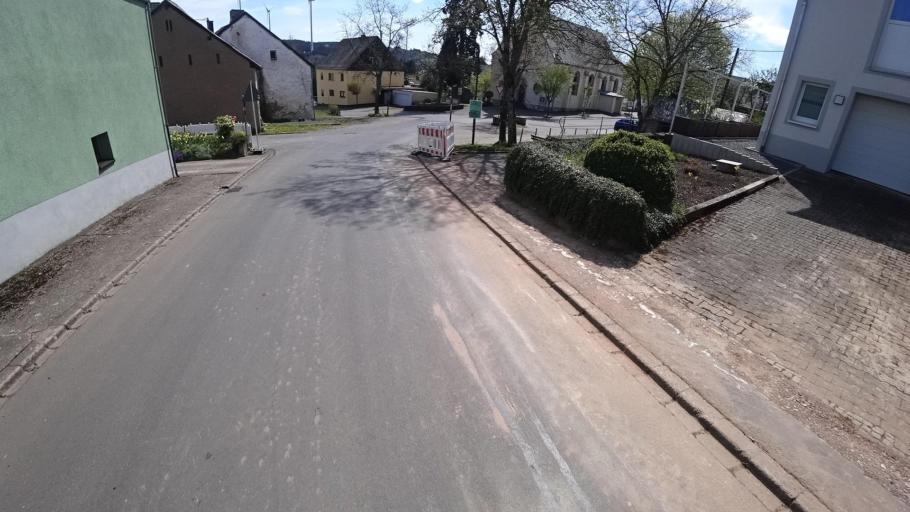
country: DE
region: Rheinland-Pfalz
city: Grimburg
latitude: 49.6213
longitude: 6.8843
